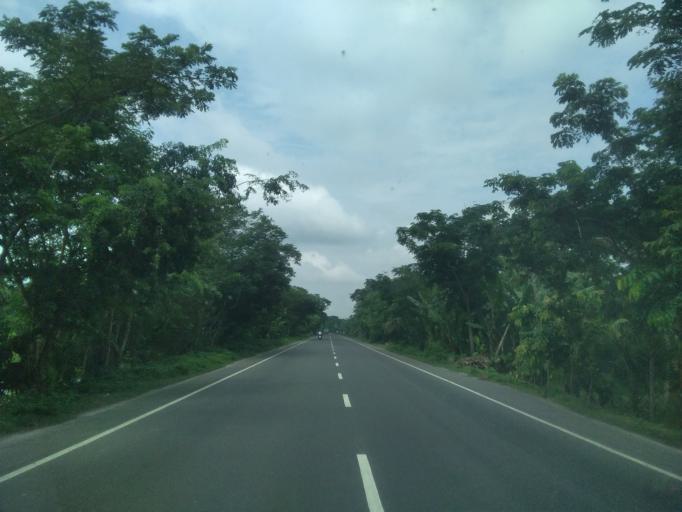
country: BD
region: Khulna
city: Kesabpur
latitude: 22.7991
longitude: 89.2297
